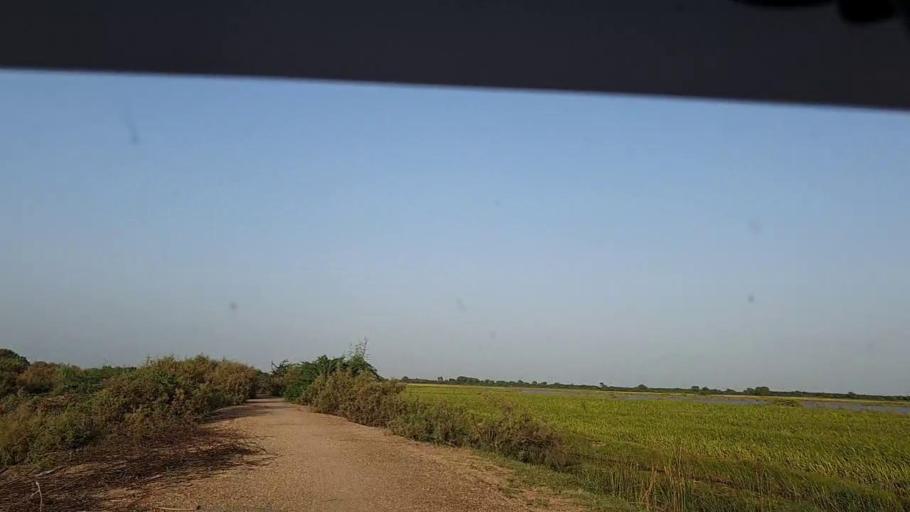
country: PK
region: Sindh
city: Kadhan
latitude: 24.5435
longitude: 68.9534
